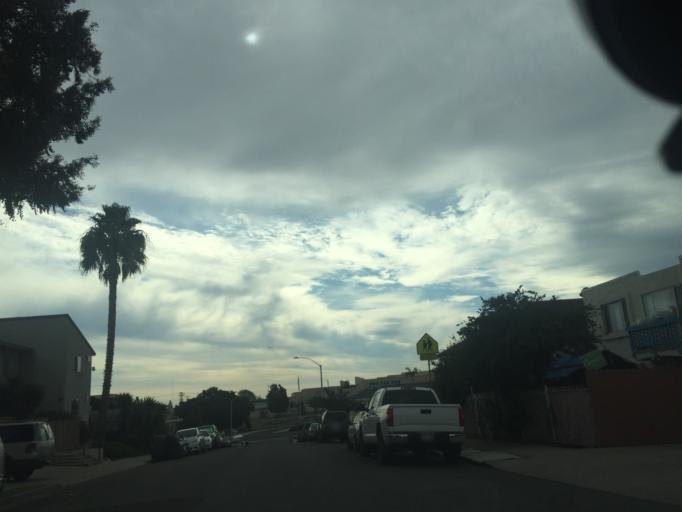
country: US
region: California
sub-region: San Diego County
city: Lemon Grove
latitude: 32.7541
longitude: -117.0891
